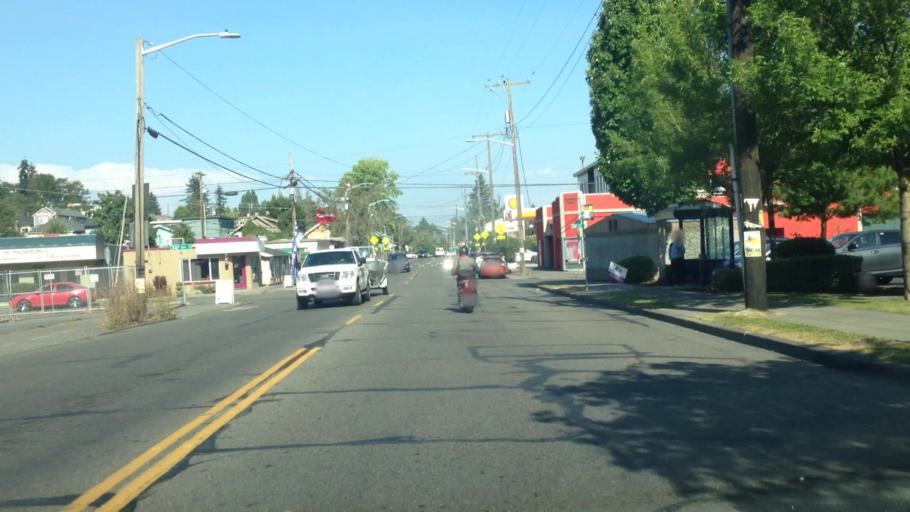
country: US
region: Washington
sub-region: King County
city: Seattle
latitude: 47.5641
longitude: -122.2878
